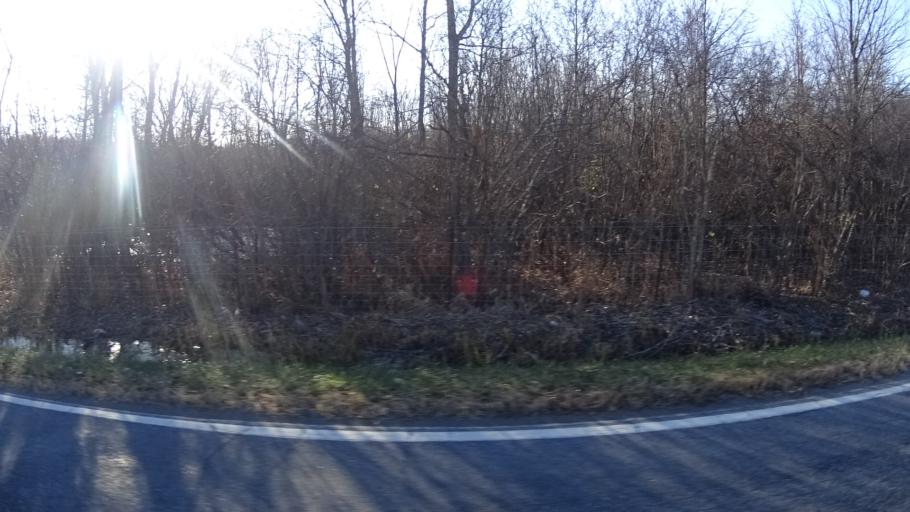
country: US
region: Ohio
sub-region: Lorain County
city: Oberlin
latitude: 41.2653
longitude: -82.2095
